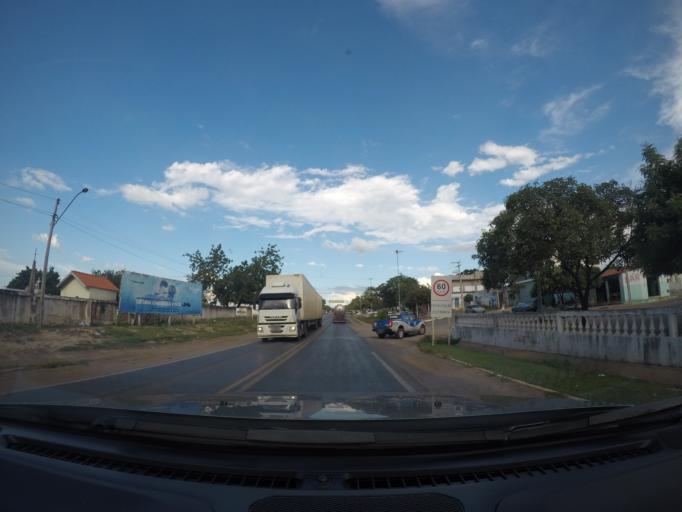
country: BR
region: Bahia
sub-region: Ibotirama
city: Ibotirama
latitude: -12.1790
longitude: -43.2220
